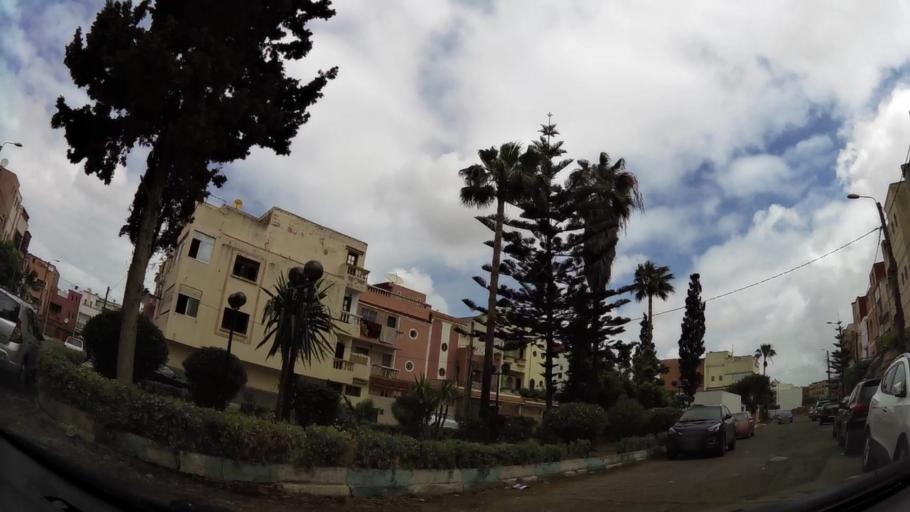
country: MA
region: Grand Casablanca
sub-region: Casablanca
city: Casablanca
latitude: 33.5338
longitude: -7.6003
